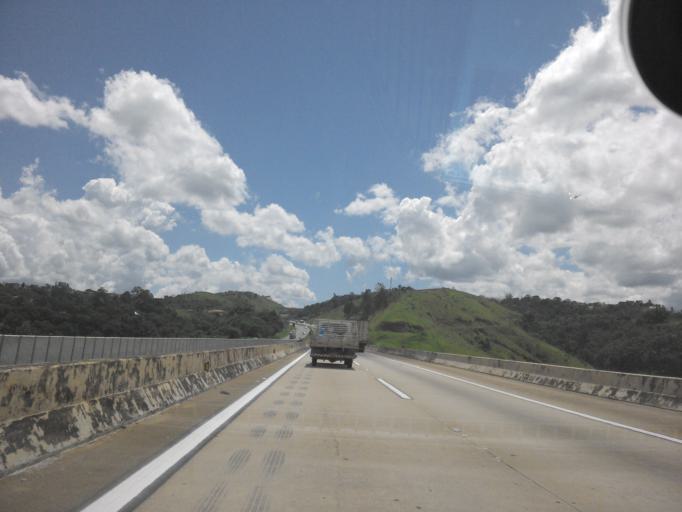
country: BR
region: Sao Paulo
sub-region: Santa Isabel
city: Santa Isabel
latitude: -23.2187
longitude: -46.1448
